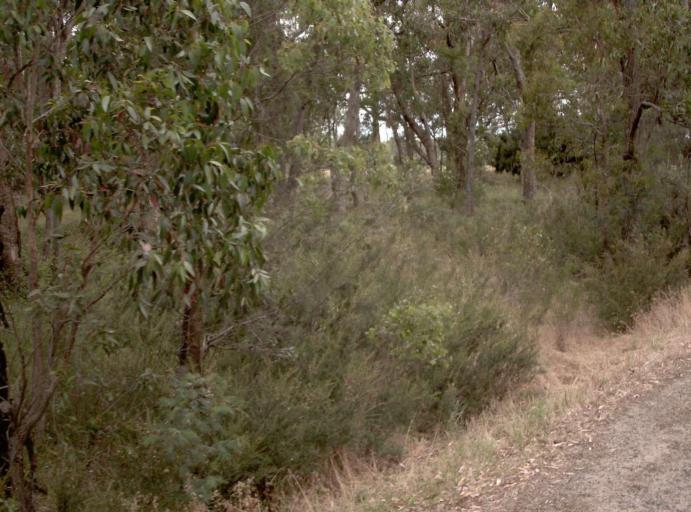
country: AU
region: Victoria
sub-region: Latrobe
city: Traralgon
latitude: -38.5149
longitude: 146.8568
